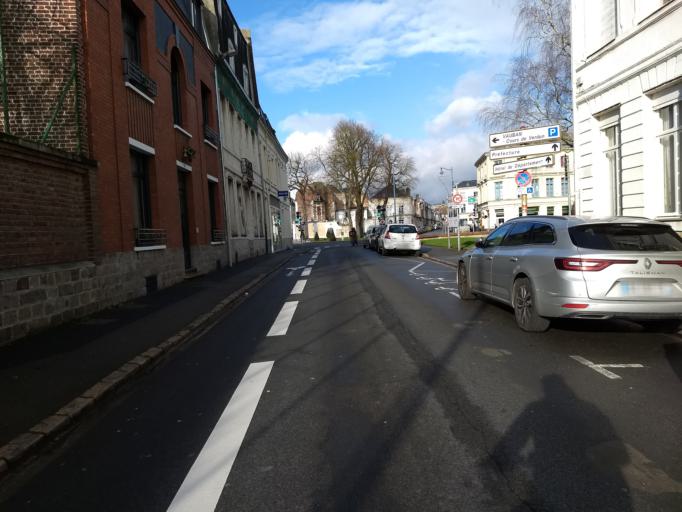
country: FR
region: Nord-Pas-de-Calais
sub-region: Departement du Pas-de-Calais
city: Arras
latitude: 50.2899
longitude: 2.7692
